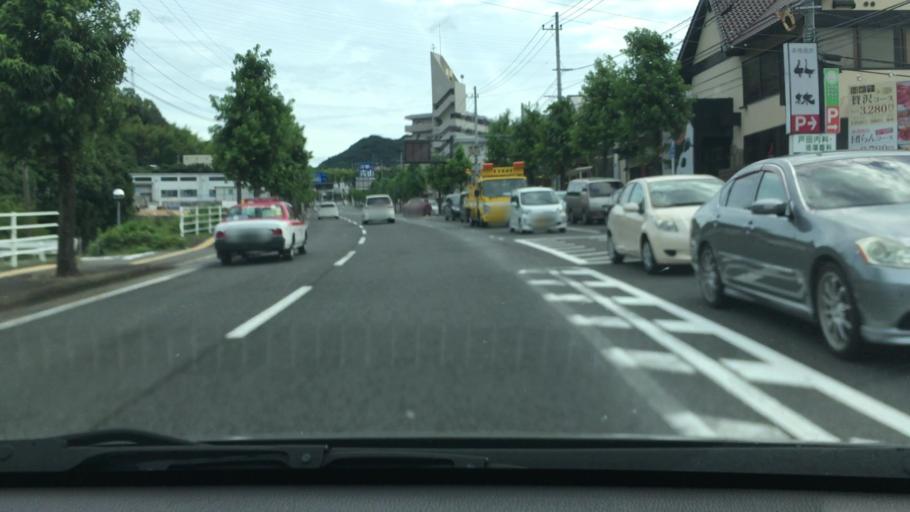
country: JP
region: Nagasaki
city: Togitsu
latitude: 32.8181
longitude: 129.8467
